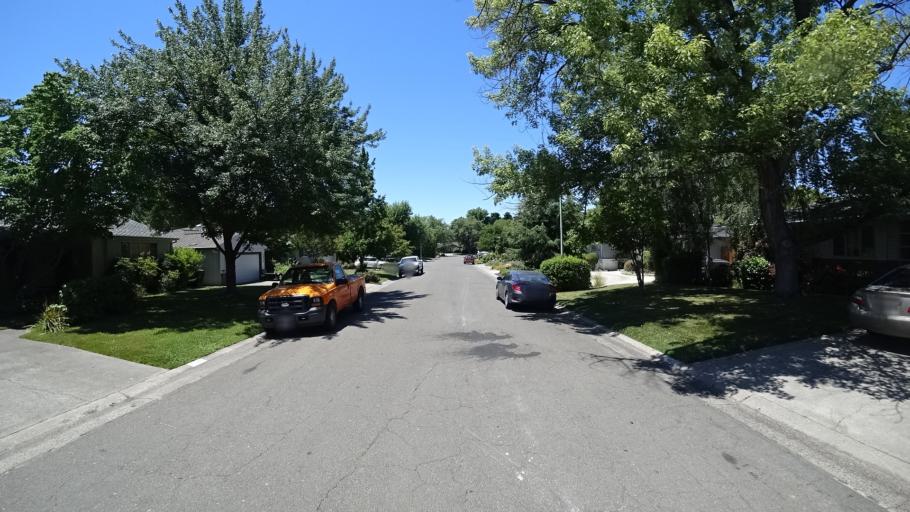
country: US
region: California
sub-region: Sacramento County
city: Sacramento
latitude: 38.5291
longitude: -121.5104
